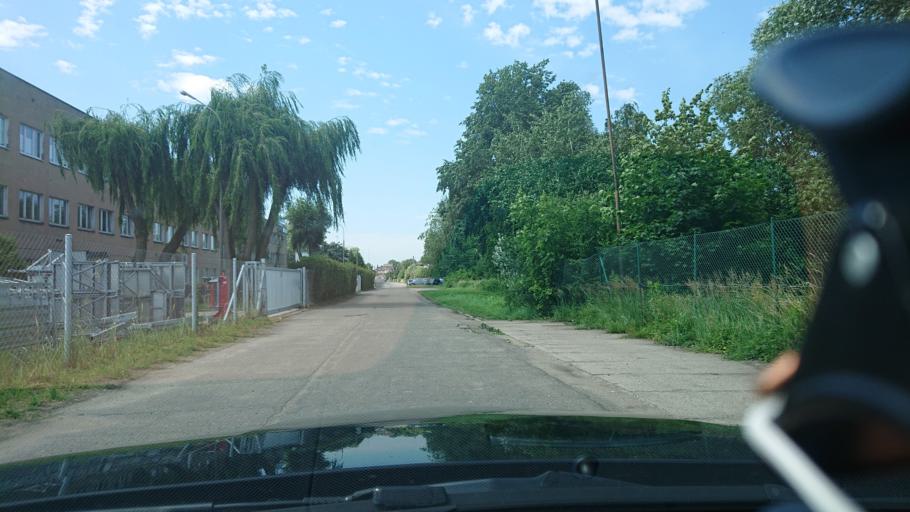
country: PL
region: Greater Poland Voivodeship
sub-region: Powiat gnieznienski
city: Gniezno
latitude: 52.5267
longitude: 17.6061
